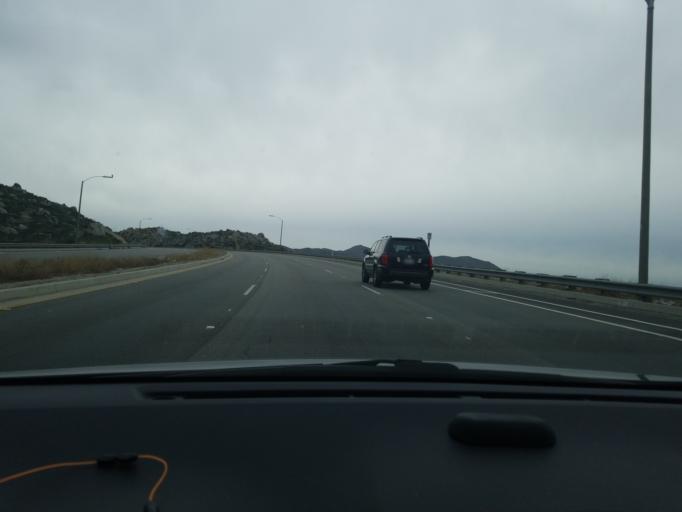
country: US
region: California
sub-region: Riverside County
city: Menifee
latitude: 33.6946
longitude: -117.1326
